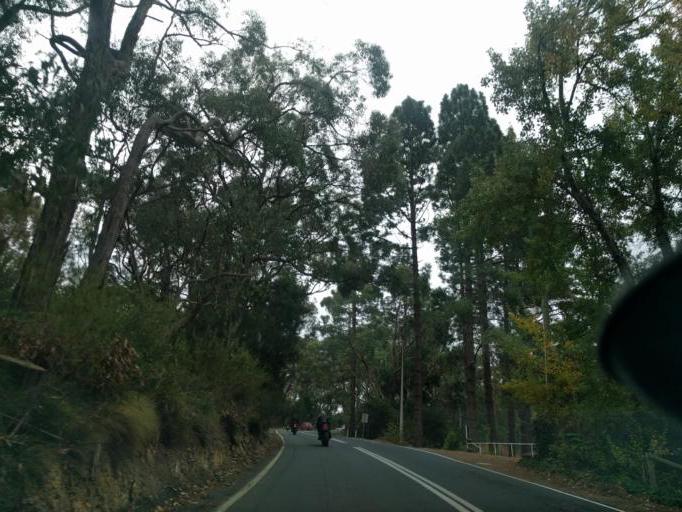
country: AU
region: South Australia
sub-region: Adelaide Hills
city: Stirling
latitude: -35.0228
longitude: 138.7545
